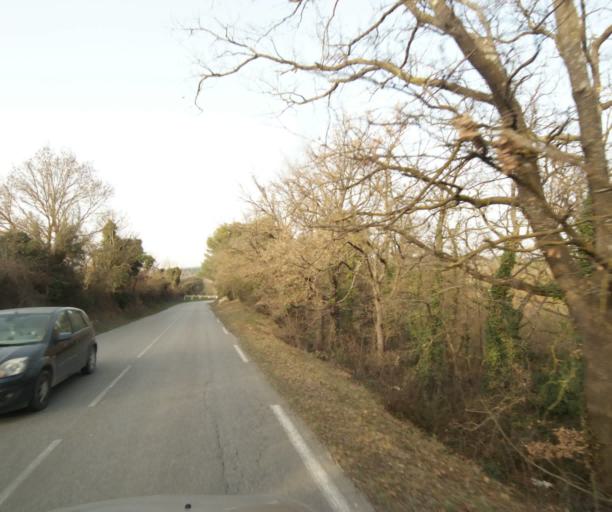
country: FR
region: Provence-Alpes-Cote d'Azur
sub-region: Departement des Bouches-du-Rhone
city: Eguilles
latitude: 43.5819
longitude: 5.3658
